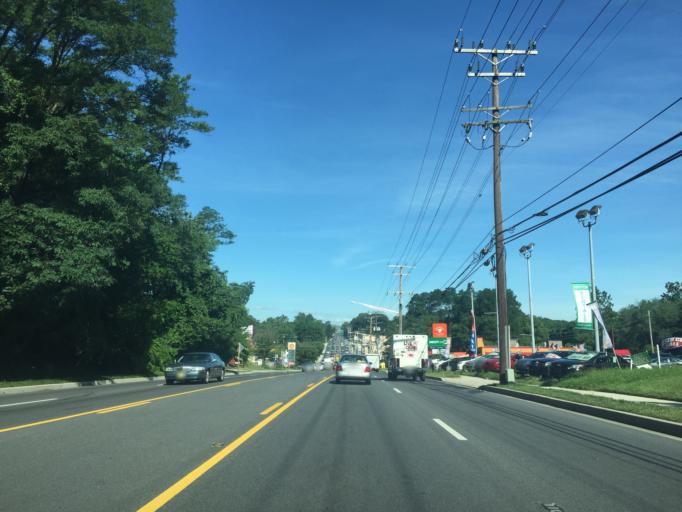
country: US
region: Maryland
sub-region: Baltimore County
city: Lochearn
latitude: 39.3439
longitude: -76.7305
